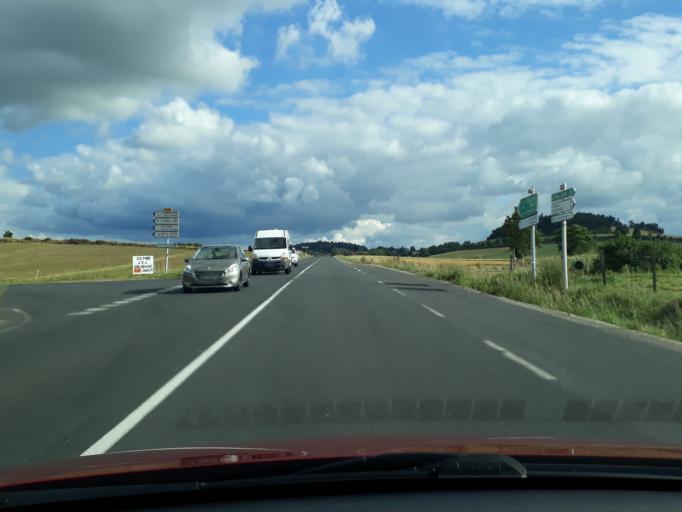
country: FR
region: Auvergne
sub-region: Departement de la Haute-Loire
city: Solignac-sur-Loire
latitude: 44.9559
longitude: 3.8435
